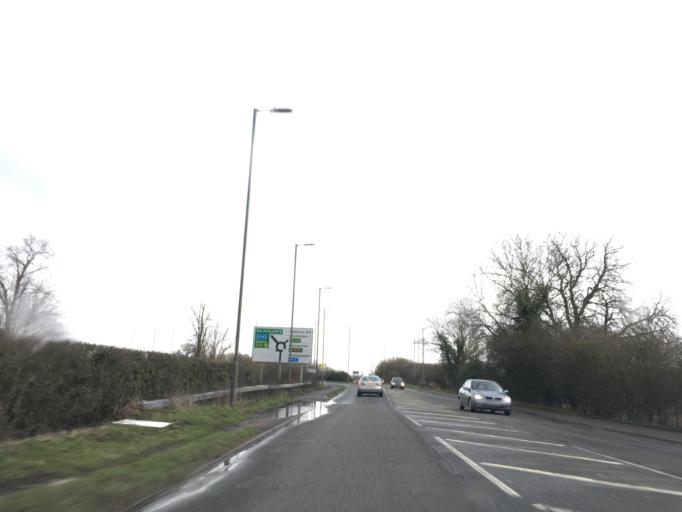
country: GB
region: England
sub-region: West Berkshire
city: Newbury
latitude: 51.4093
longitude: -1.3594
